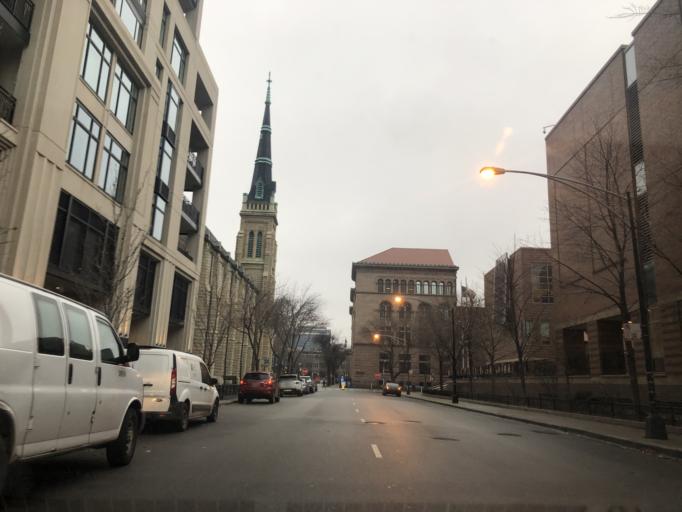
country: US
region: Illinois
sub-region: Cook County
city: Chicago
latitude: 41.8999
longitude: -87.6286
